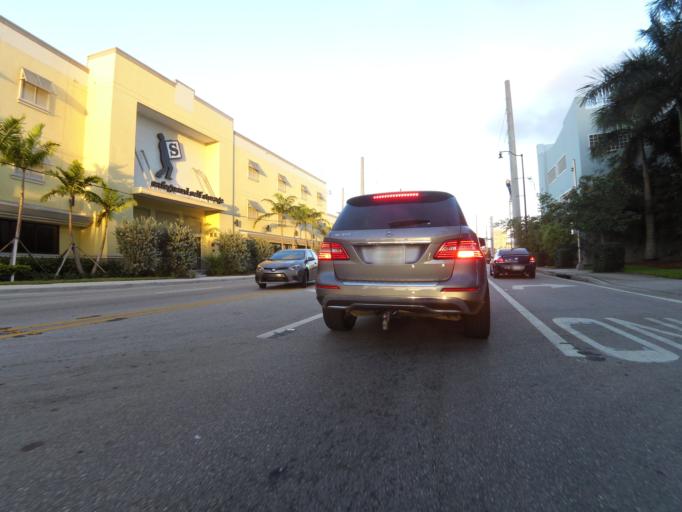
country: US
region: Florida
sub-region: Miami-Dade County
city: Allapattah
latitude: 25.8102
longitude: -80.2041
